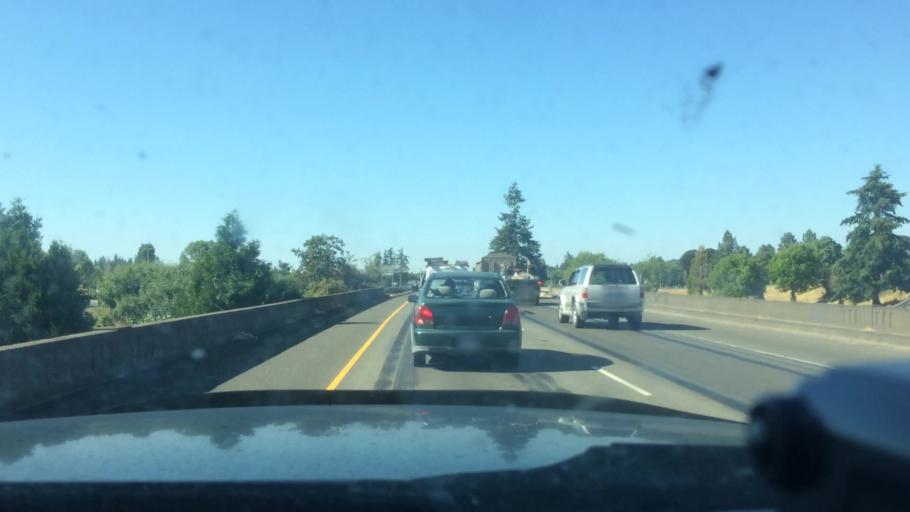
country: US
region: Oregon
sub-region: Linn County
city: Millersburg
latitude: 44.6436
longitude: -123.0625
